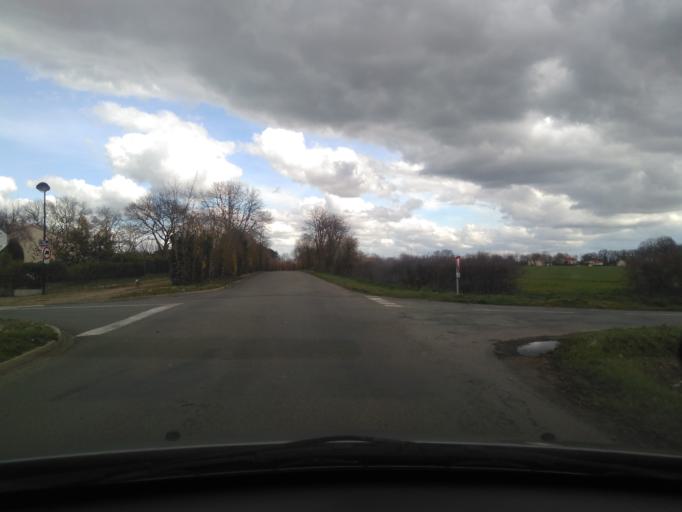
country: FR
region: Pays de la Loire
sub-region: Departement de la Vendee
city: Les Essarts
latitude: 46.7652
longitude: -1.2335
